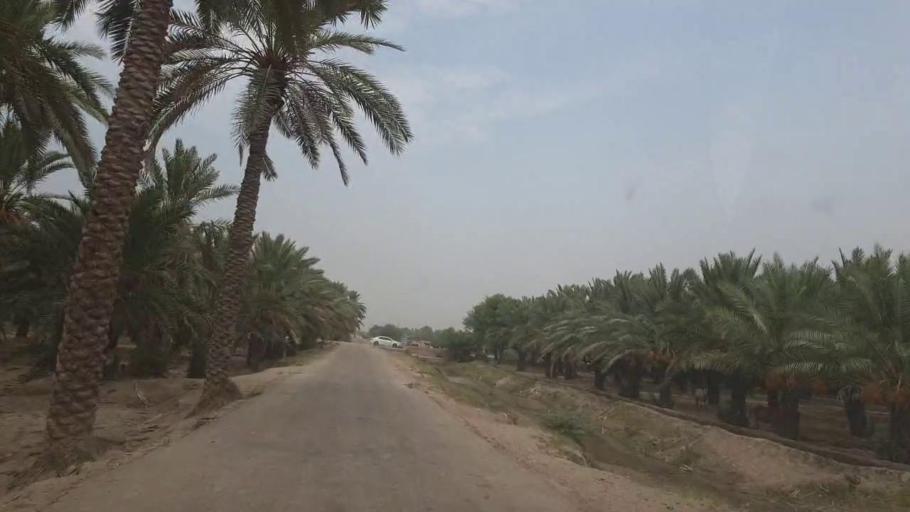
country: PK
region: Sindh
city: Kot Diji
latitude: 27.4301
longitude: 68.7009
